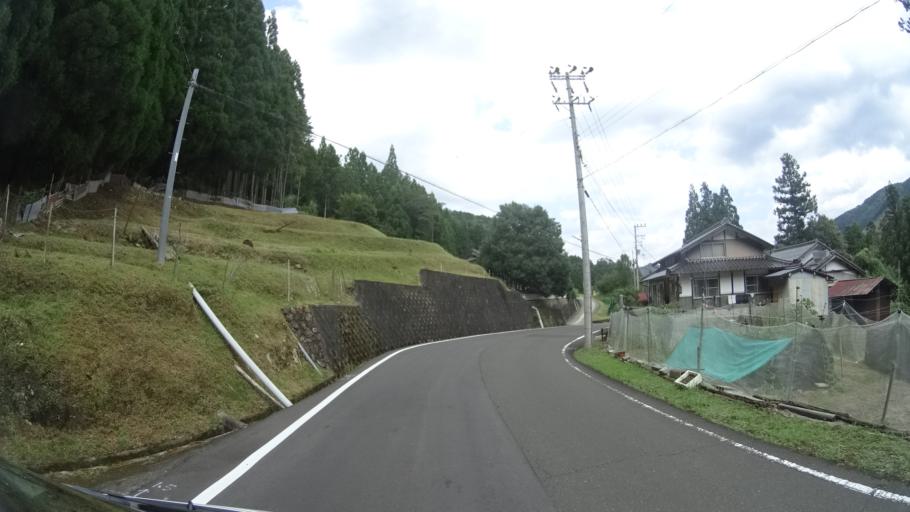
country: JP
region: Kyoto
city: Ayabe
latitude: 35.2779
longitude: 135.3305
